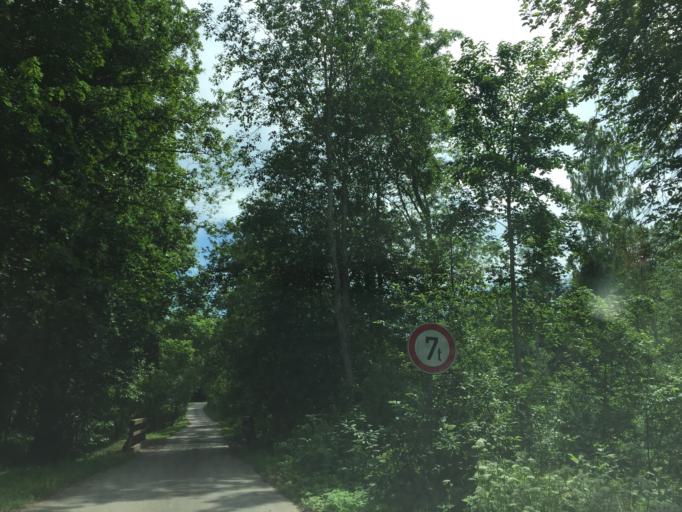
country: LV
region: Engure
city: Smarde
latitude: 57.0268
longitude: 23.2531
